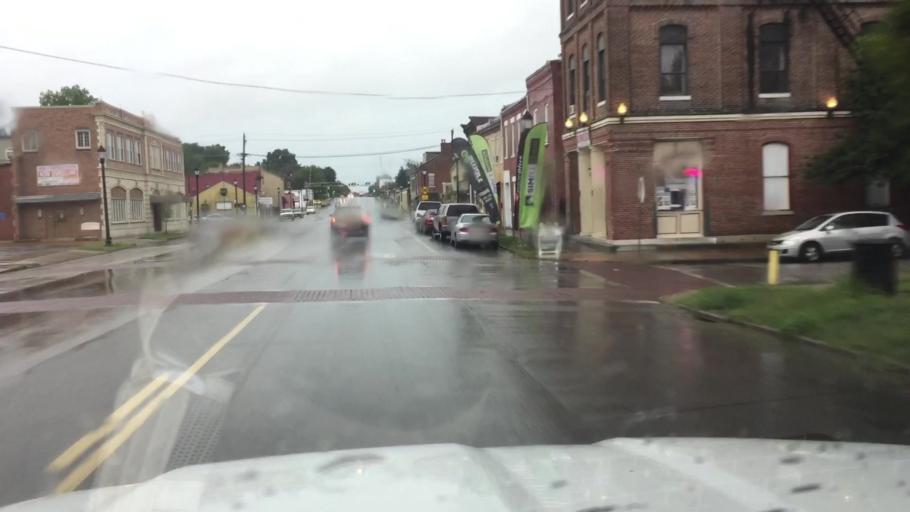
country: US
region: Missouri
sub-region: Saint Louis County
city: Lemay
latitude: 38.5462
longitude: -90.2594
